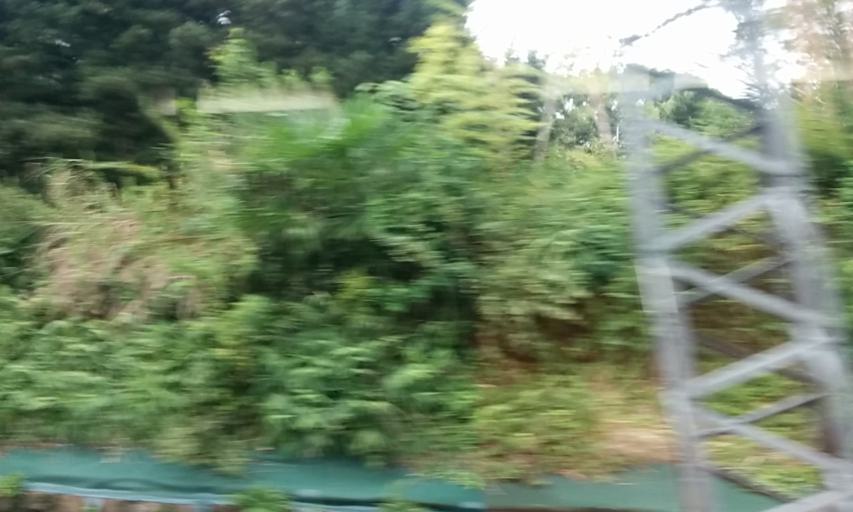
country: JP
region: Nara
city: Tawaramoto
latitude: 34.6117
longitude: 135.7815
